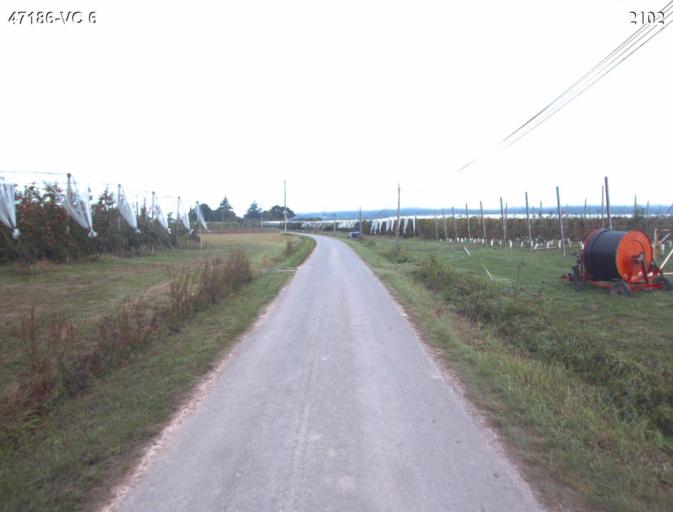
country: FR
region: Aquitaine
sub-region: Departement du Lot-et-Garonne
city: Sainte-Colombe-en-Bruilhois
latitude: 44.2193
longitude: 0.4600
